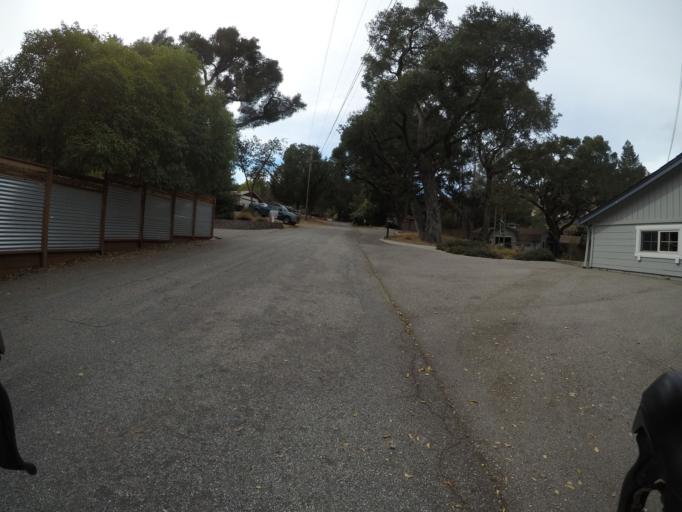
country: US
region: California
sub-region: Santa Cruz County
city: Mount Hermon
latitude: 37.0681
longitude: -122.0609
